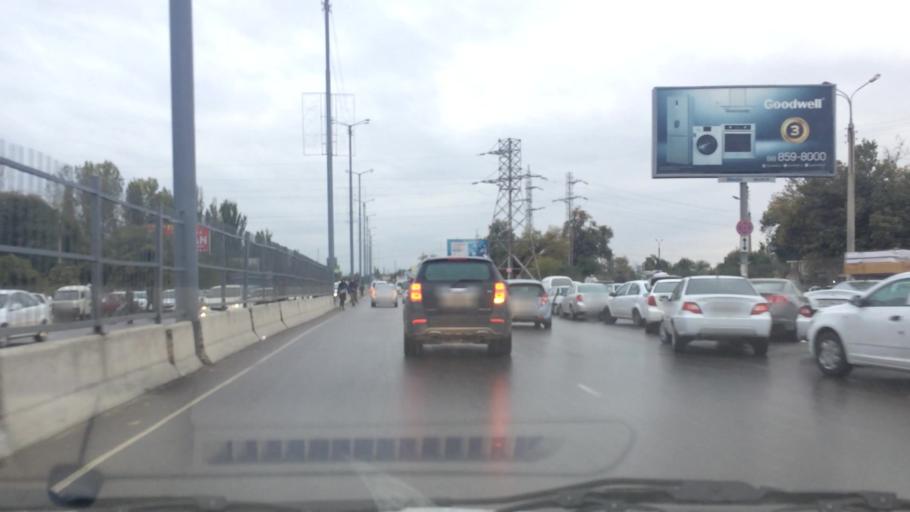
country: UZ
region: Toshkent Shahri
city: Tashkent
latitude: 41.2420
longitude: 69.1712
